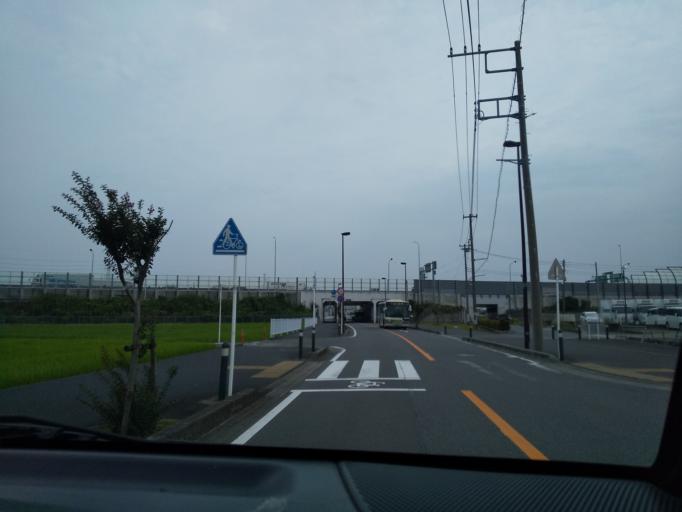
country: JP
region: Kanagawa
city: Atsugi
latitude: 35.4265
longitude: 139.3908
